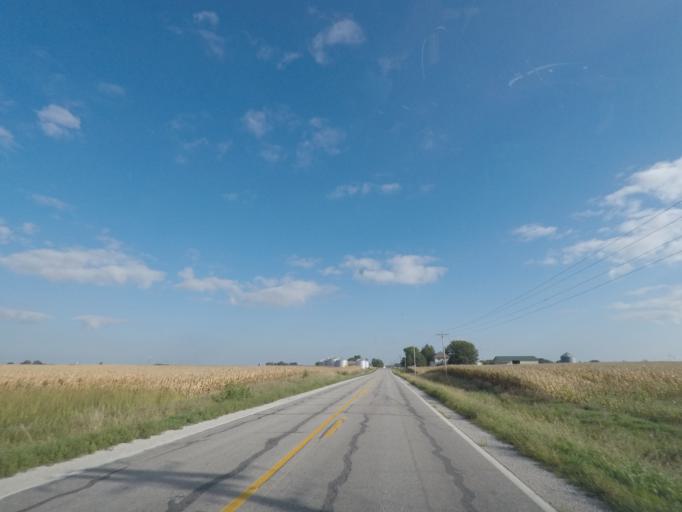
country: US
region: Iowa
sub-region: Story County
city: Nevada
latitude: 41.9951
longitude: -93.4629
